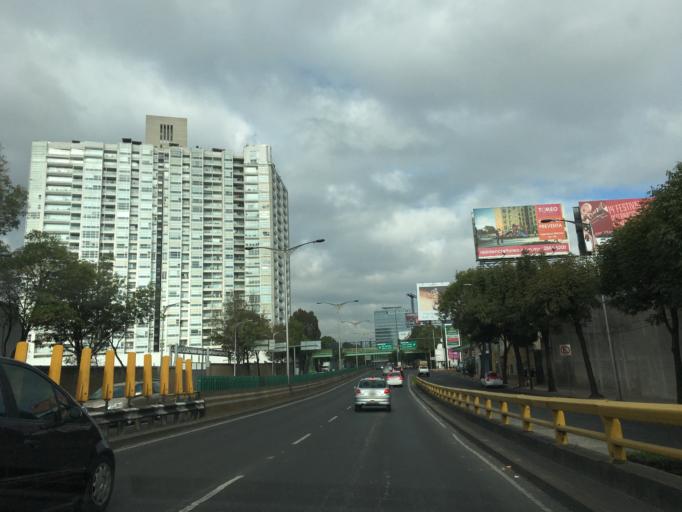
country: MX
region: Mexico City
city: Miguel Hidalgo
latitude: 19.4449
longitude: -99.2005
